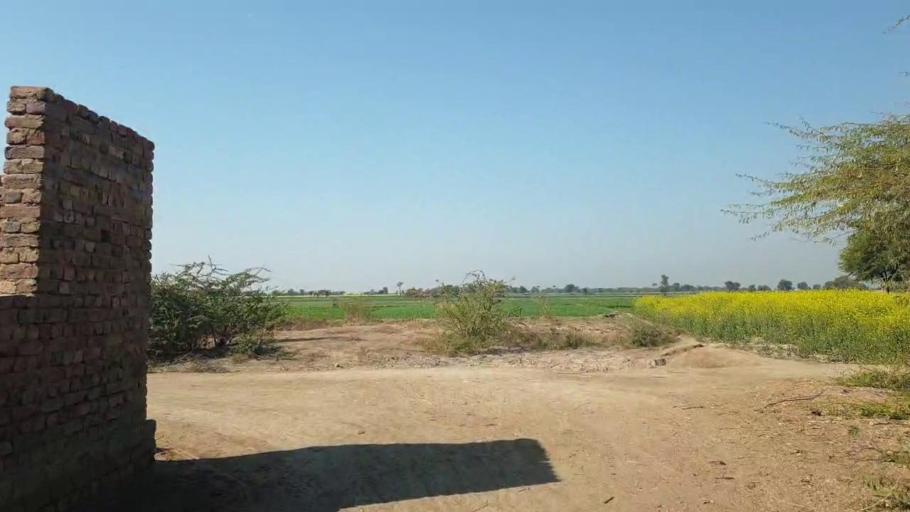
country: PK
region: Sindh
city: Shahpur Chakar
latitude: 26.0761
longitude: 68.6427
